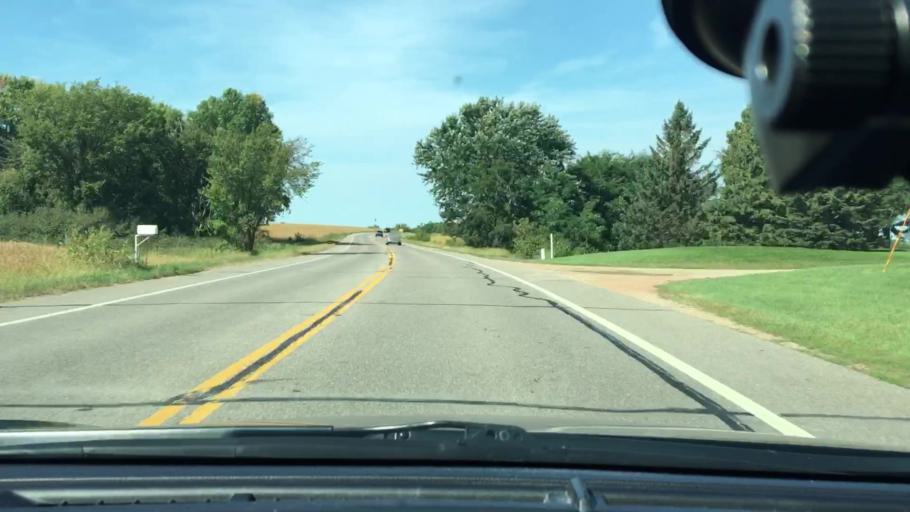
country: US
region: Minnesota
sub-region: Hennepin County
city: Corcoran
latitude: 45.0910
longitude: -93.5366
